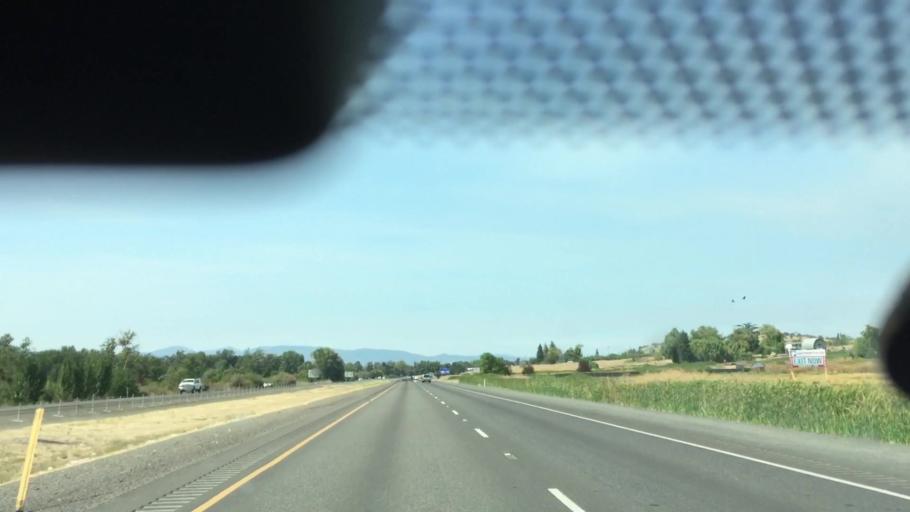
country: US
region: Oregon
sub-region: Jackson County
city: Talent
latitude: 42.2389
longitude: -122.7622
